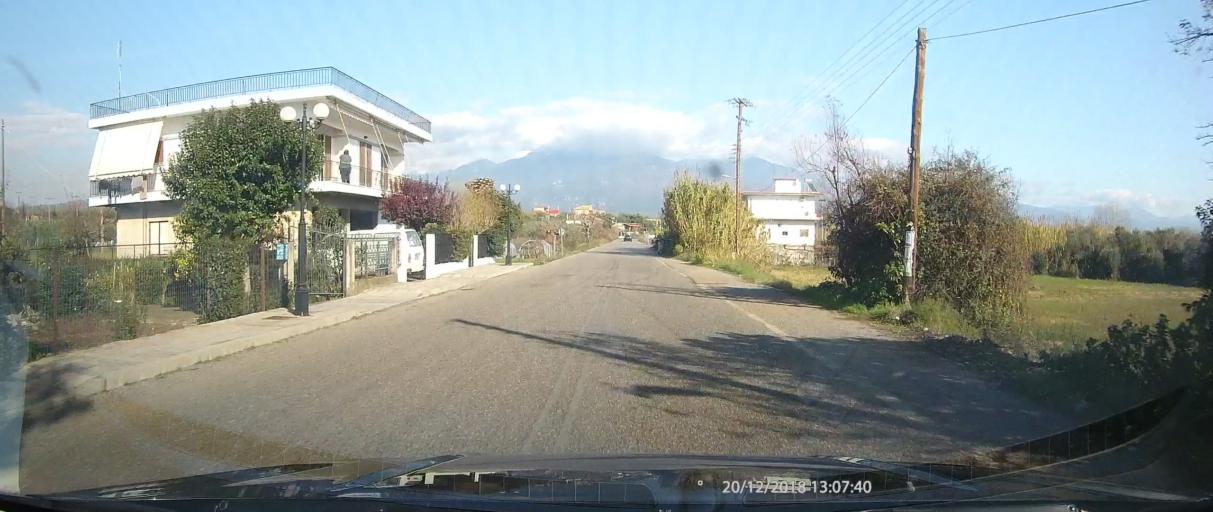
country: GR
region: West Greece
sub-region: Nomos Aitolias kai Akarnanias
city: Panaitolion
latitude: 38.5902
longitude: 21.4585
